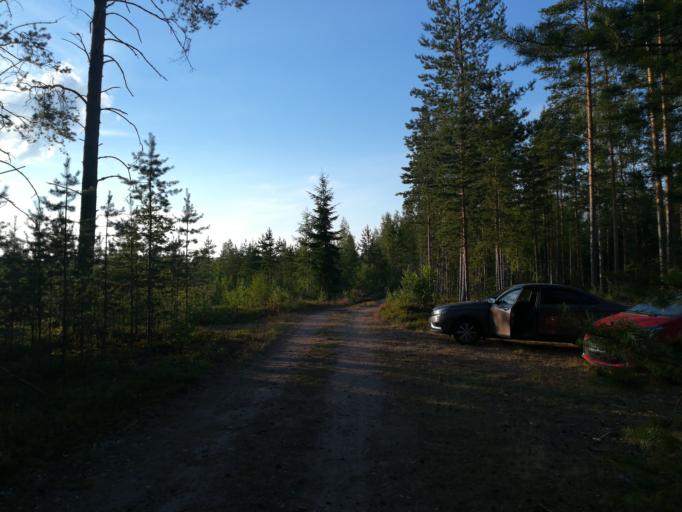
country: FI
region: Southern Savonia
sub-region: Mikkeli
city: Puumala
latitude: 61.4280
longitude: 28.4566
